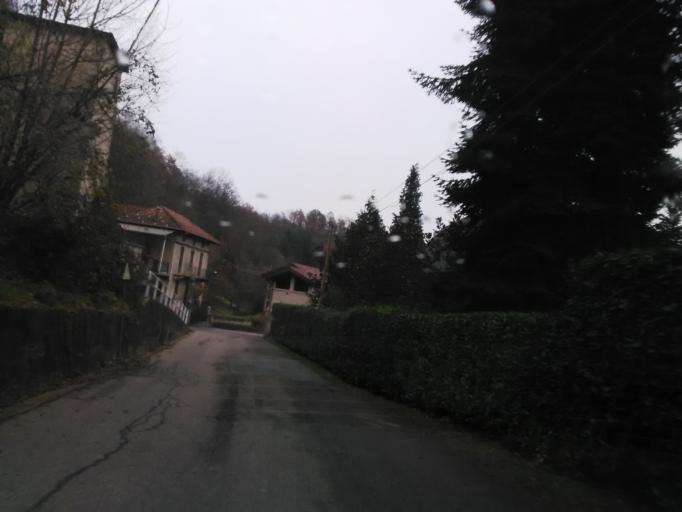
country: IT
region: Piedmont
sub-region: Provincia di Biella
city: Pray
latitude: 45.6773
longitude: 8.2136
